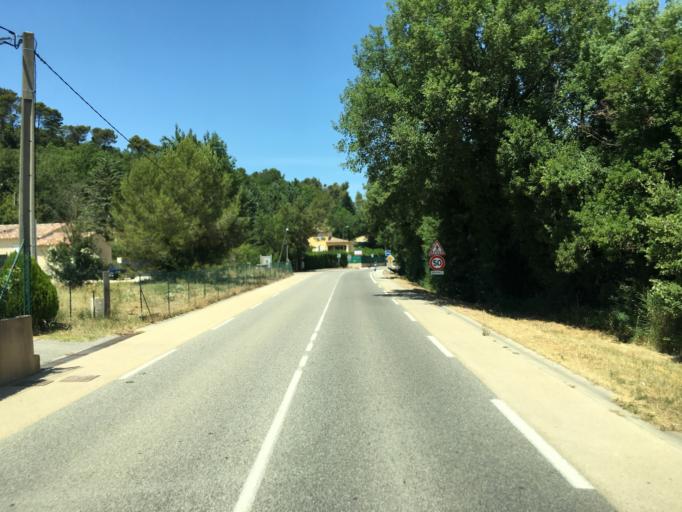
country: FR
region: Provence-Alpes-Cote d'Azur
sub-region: Departement du Var
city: Saint-Maximin-la-Sainte-Baume
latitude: 43.4735
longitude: 5.8343
